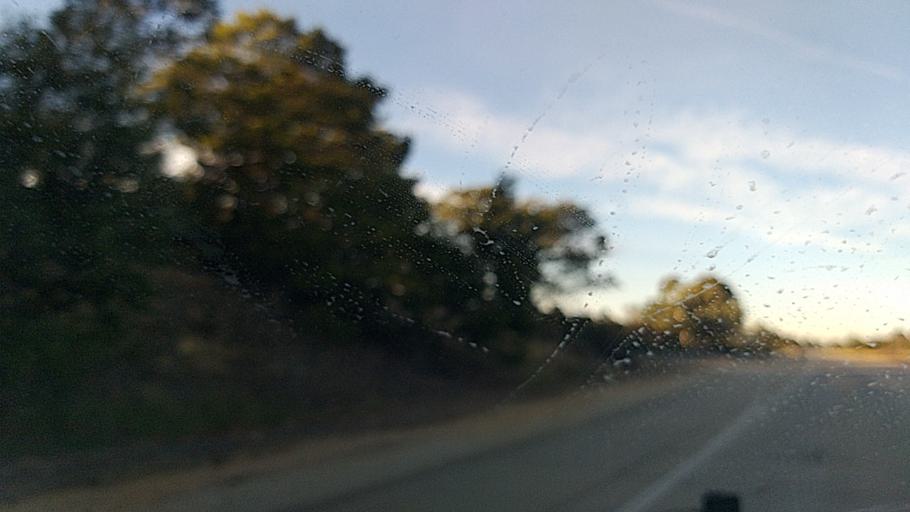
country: AU
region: New South Wales
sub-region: Yass Valley
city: Gundaroo
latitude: -35.1262
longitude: 149.3430
